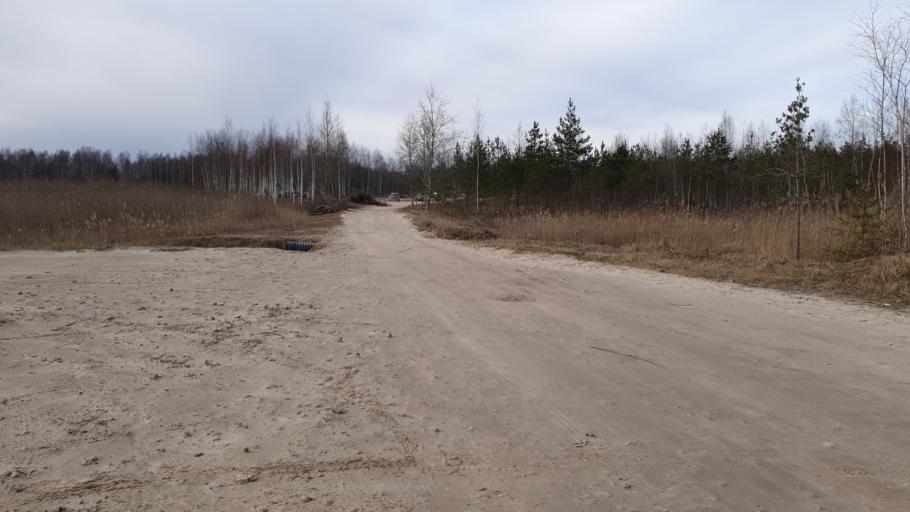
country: LV
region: Olaine
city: Olaine
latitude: 56.7884
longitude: 23.8725
